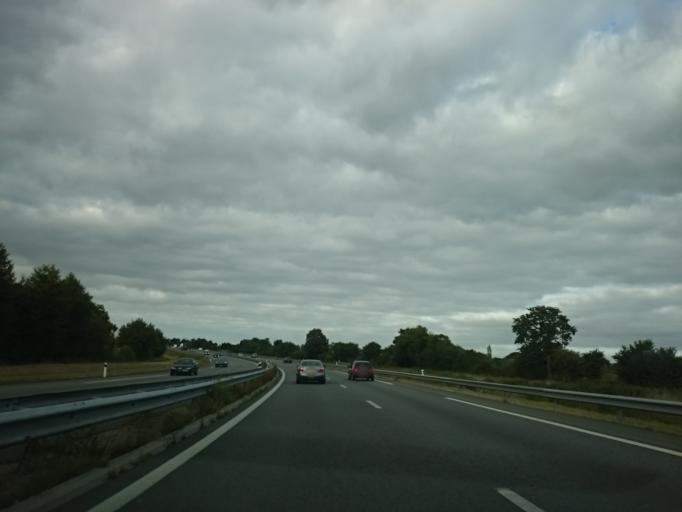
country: FR
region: Brittany
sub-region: Departement d'Ille-et-Vilaine
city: La Dominelais
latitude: 47.7766
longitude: -1.7001
